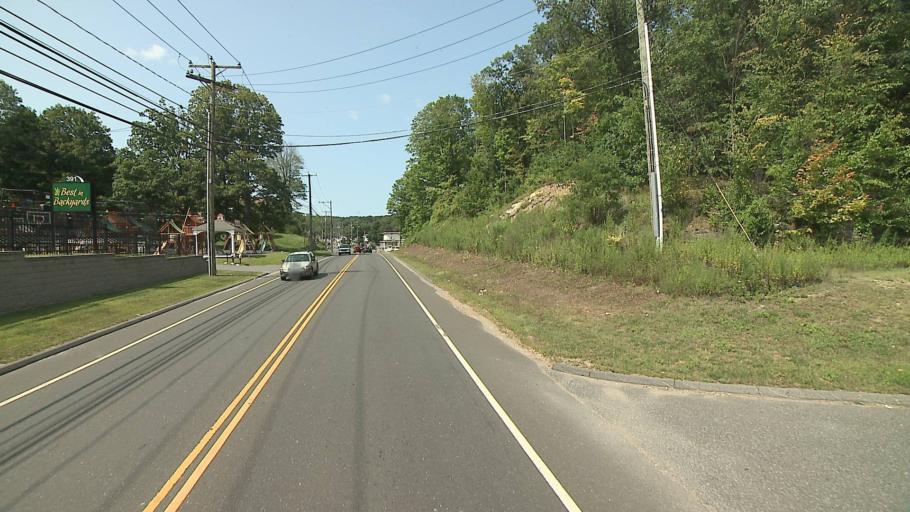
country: US
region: Connecticut
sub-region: Fairfield County
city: Trumbull
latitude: 41.3196
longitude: -73.2626
